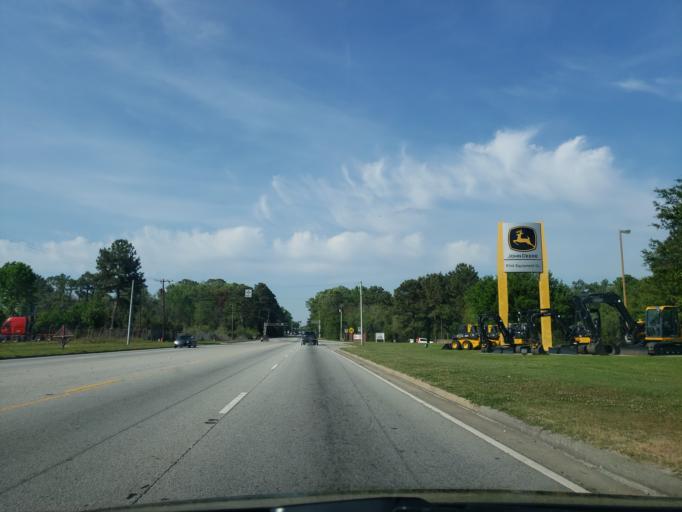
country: US
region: Georgia
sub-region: Chatham County
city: Garden City
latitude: 32.0879
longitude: -81.1972
